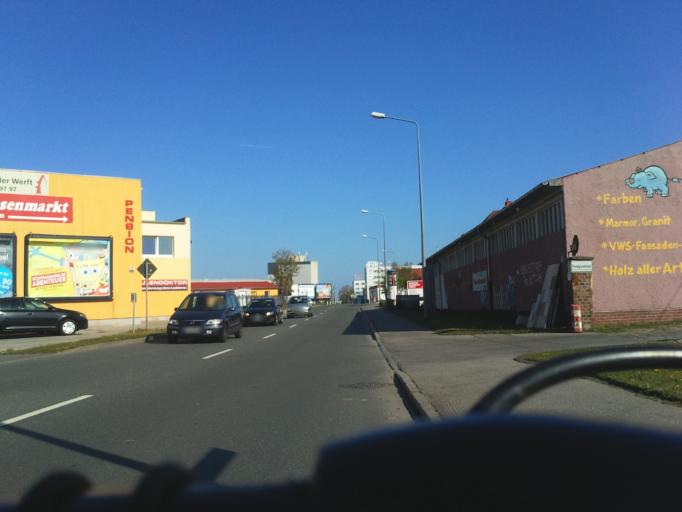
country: DE
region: Mecklenburg-Vorpommern
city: Rostock
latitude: 54.0963
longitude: 12.0987
